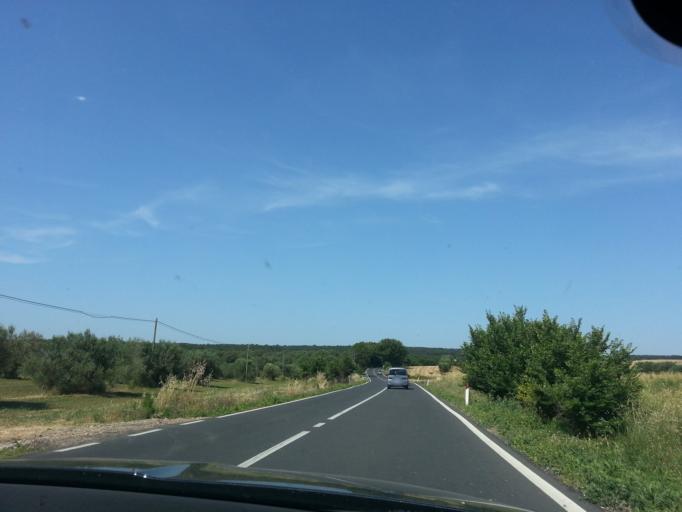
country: IT
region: Latium
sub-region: Provincia di Viterbo
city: Monte Romano
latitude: 42.2631
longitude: 11.8602
